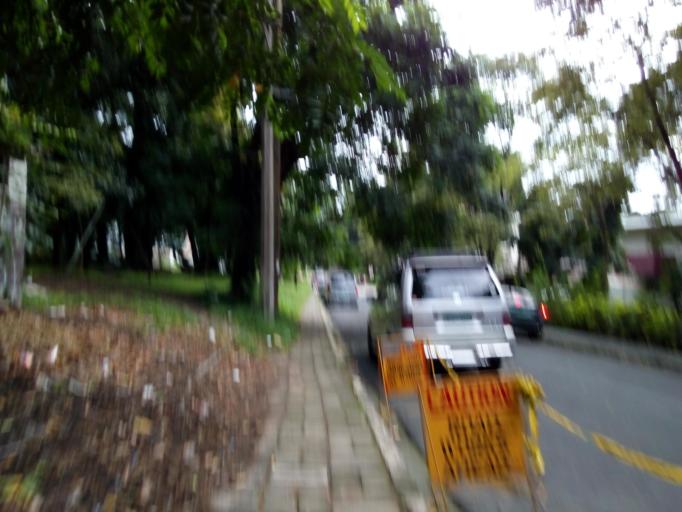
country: PH
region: Metro Manila
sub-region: Quezon City
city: Quezon City
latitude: 14.6584
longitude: 121.0706
